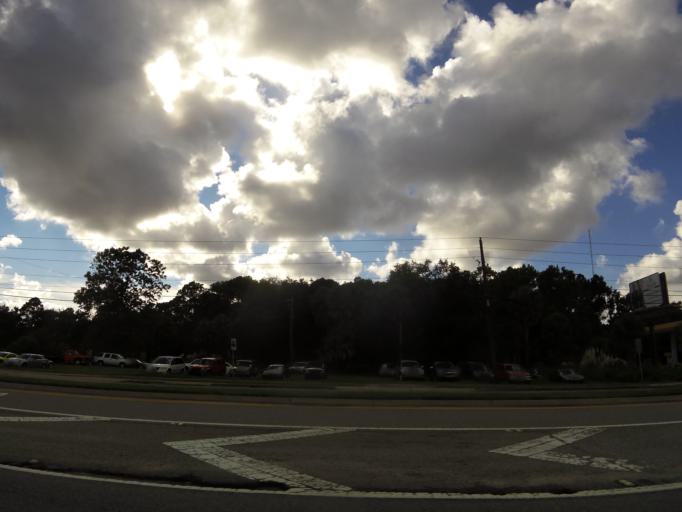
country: US
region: Georgia
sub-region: Glynn County
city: Country Club Estates
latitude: 31.1792
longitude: -81.4723
